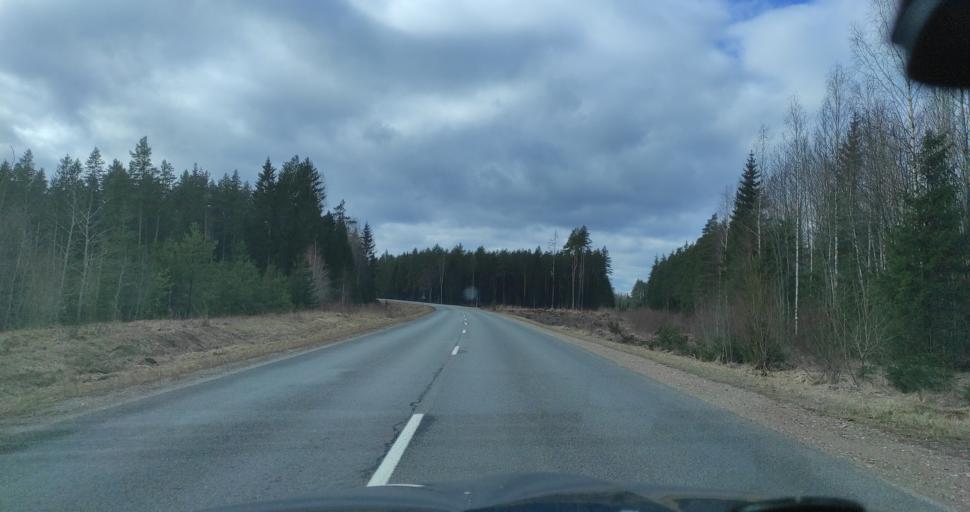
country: LV
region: Talsu Rajons
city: Stende
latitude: 57.1240
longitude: 22.5313
